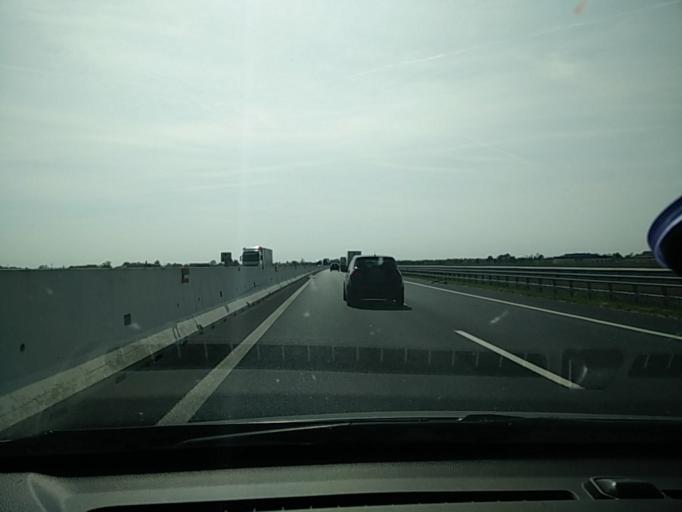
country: IT
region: Veneto
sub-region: Provincia di Venezia
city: Santo Stino di Livenza
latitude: 45.7509
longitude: 12.7236
